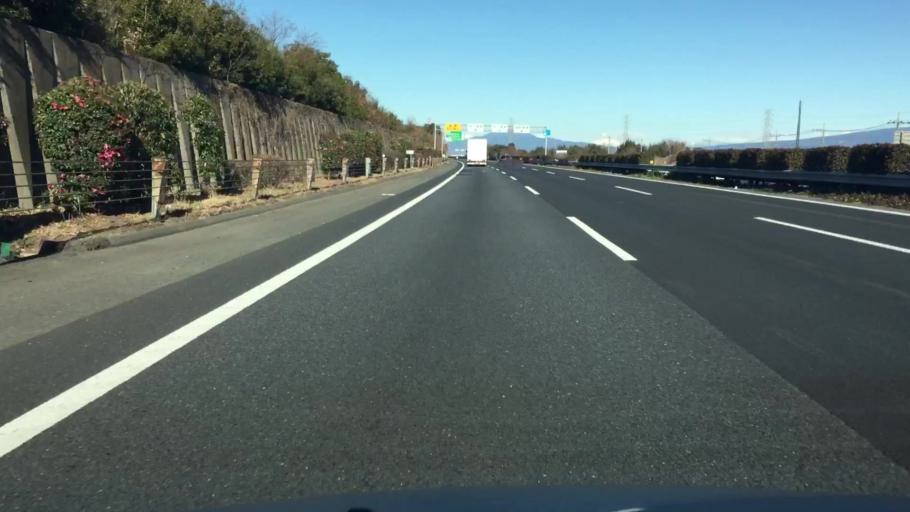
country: JP
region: Gunma
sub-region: Sawa-gun
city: Tamamura
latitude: 36.2976
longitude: 139.0963
